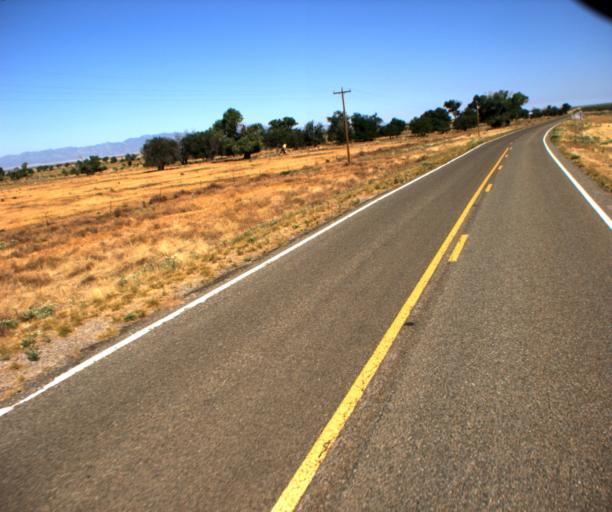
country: US
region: Arizona
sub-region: Graham County
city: Swift Trail Junction
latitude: 32.5849
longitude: -109.9618
